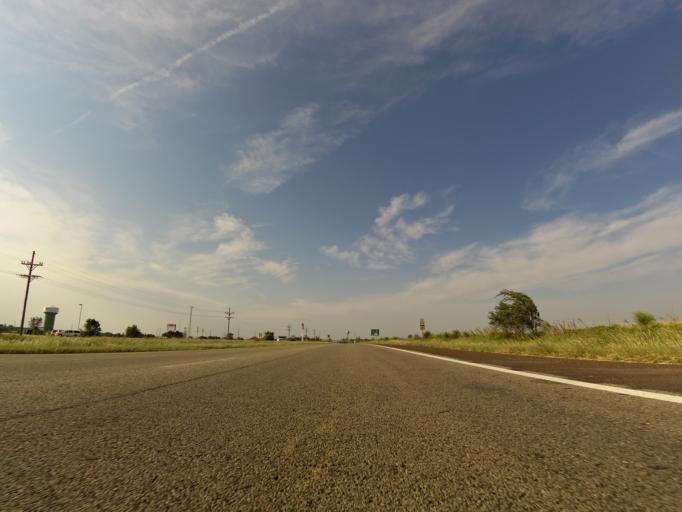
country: US
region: Kansas
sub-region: Reno County
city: South Hutchinson
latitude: 38.0081
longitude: -97.9401
